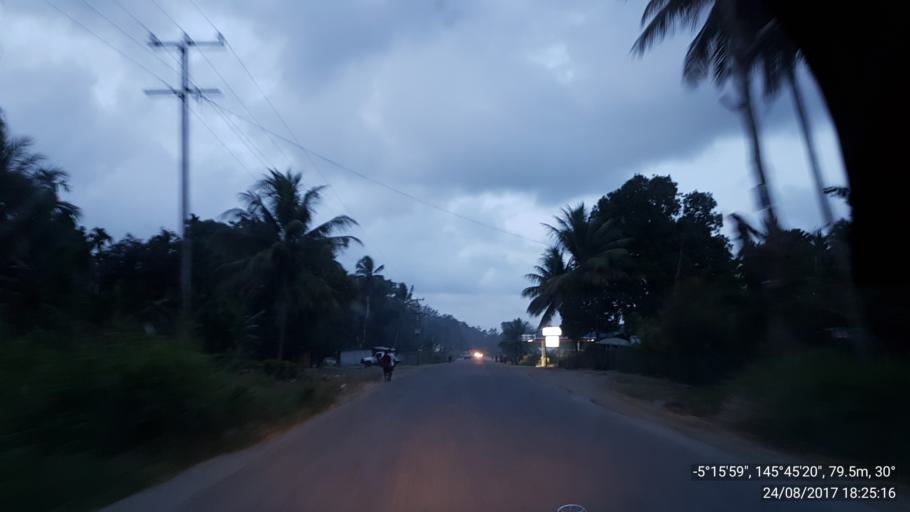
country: PG
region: Madang
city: Madang
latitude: -5.2667
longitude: 145.7558
